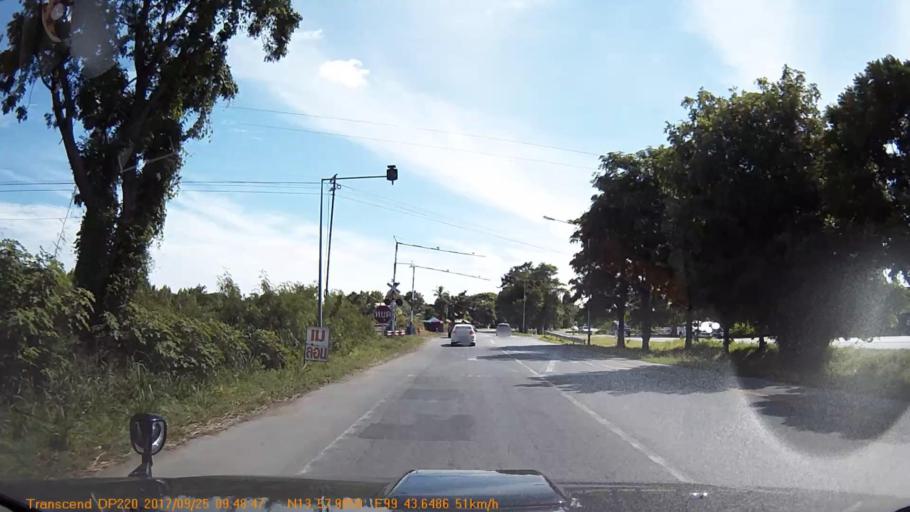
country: TH
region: Kanchanaburi
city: Tha Maka
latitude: 13.9665
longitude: 99.7276
